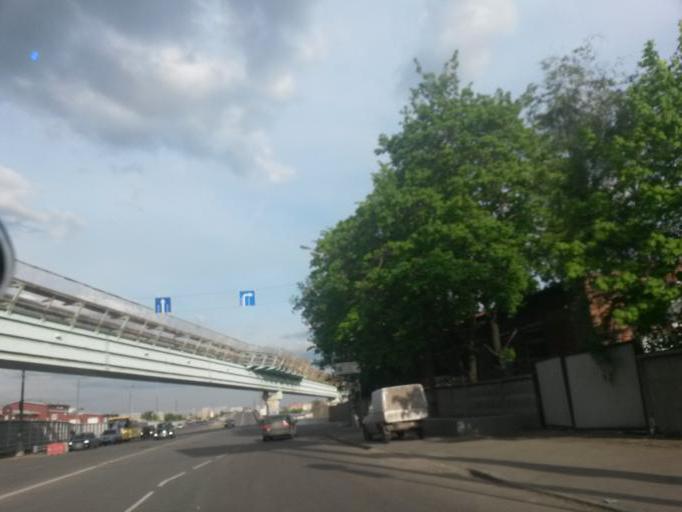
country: RU
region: Moscow
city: Taganskiy
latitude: 55.7220
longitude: 37.7007
